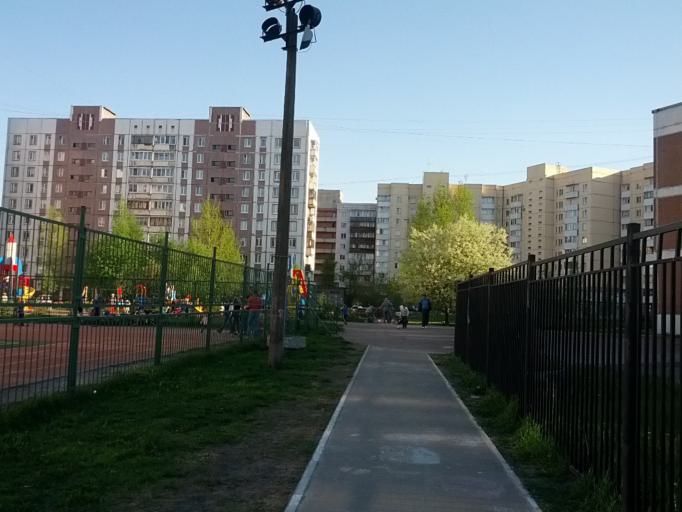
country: RU
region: Leningrad
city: Rybatskoye
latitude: 59.8987
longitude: 30.4940
